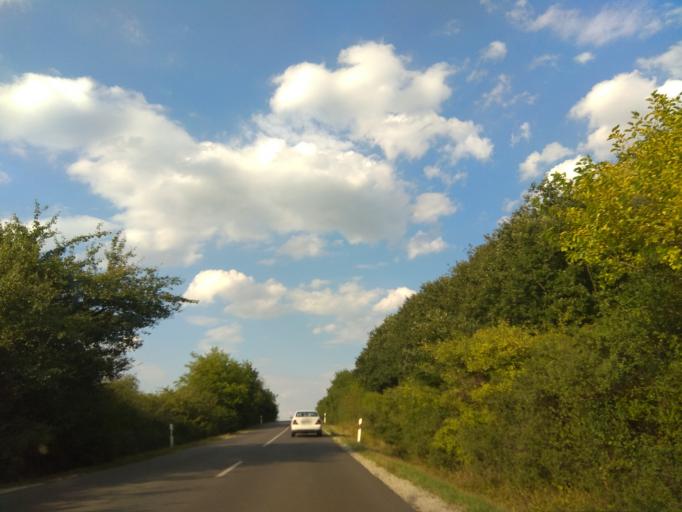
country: HU
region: Borsod-Abauj-Zemplen
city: Harsany
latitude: 47.9871
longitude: 20.7499
